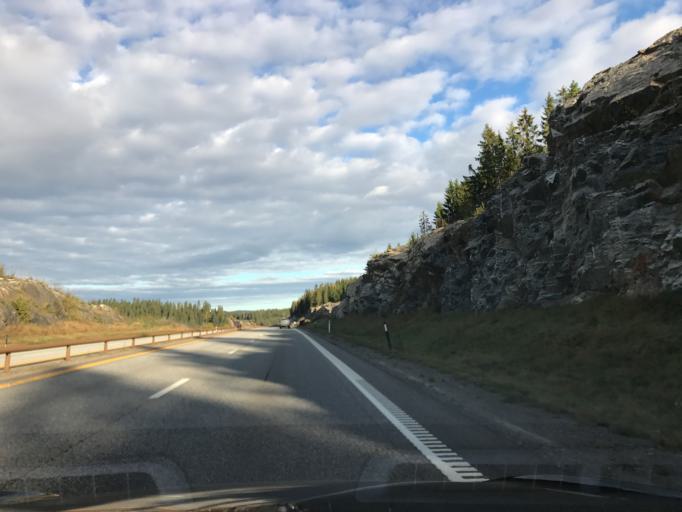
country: NO
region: Akershus
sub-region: Eidsvoll
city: Raholt
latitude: 60.2579
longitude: 11.1777
